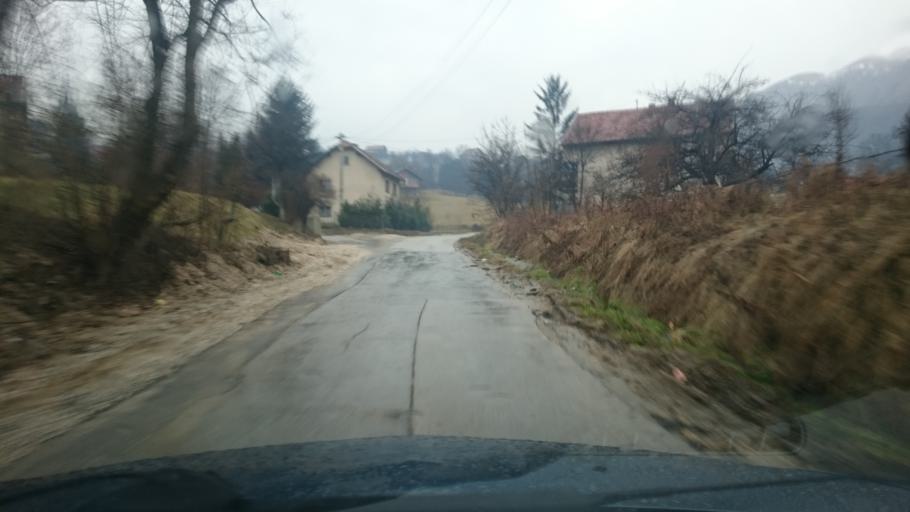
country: BA
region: Federation of Bosnia and Herzegovina
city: Travnik
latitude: 44.2205
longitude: 17.6736
